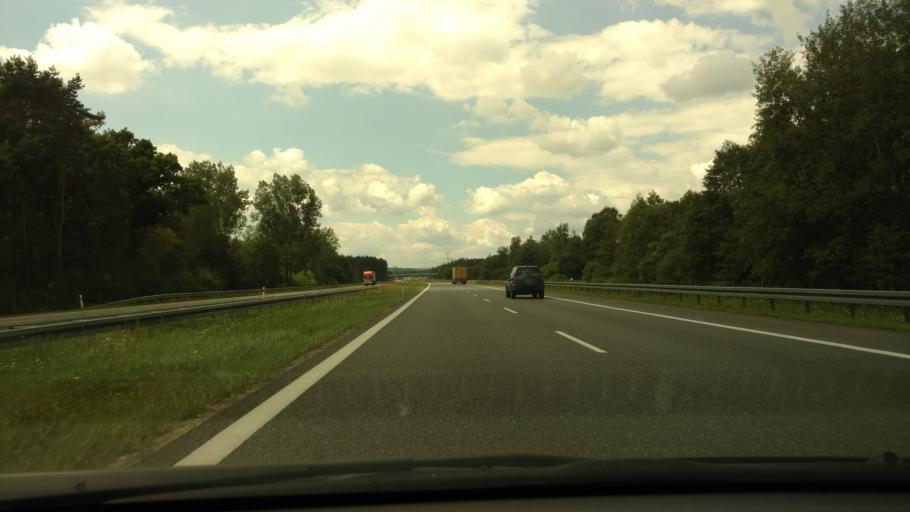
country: PL
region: Silesian Voivodeship
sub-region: Jaworzno
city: Jaworzno
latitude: 50.1498
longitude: 19.2797
